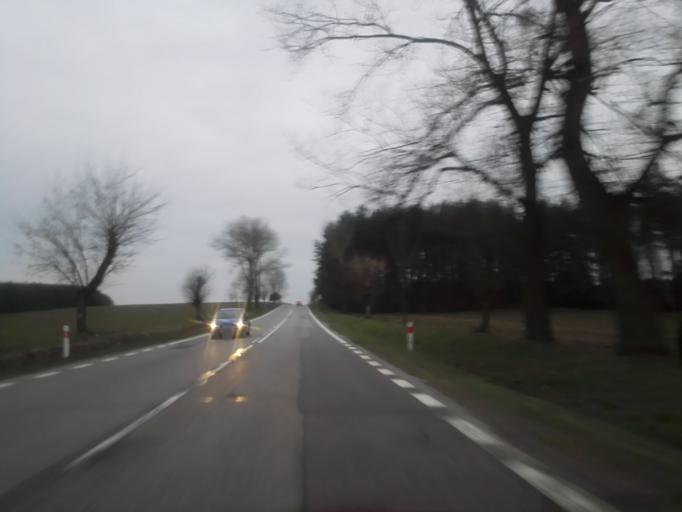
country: PL
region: Podlasie
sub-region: Powiat lomzynski
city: Piatnica
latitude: 53.2834
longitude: 22.1394
